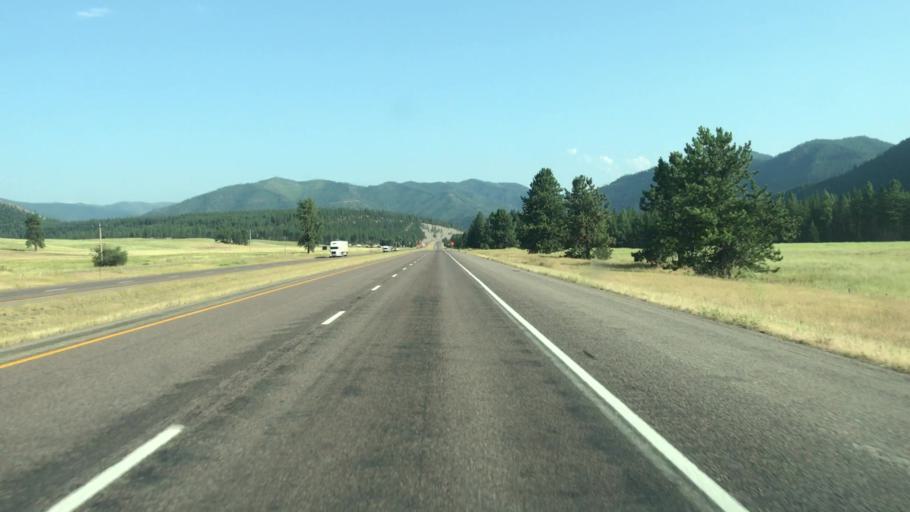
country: US
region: Montana
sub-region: Mineral County
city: Superior
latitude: 47.0406
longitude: -114.7493
